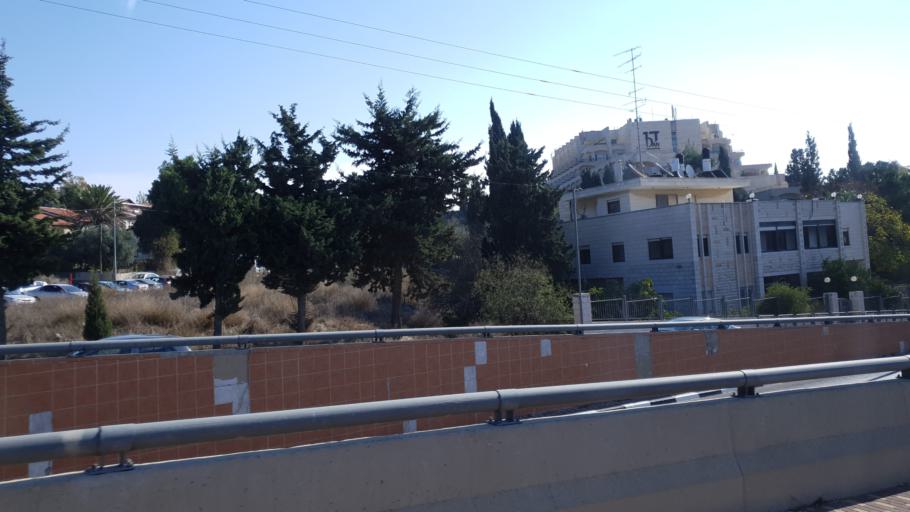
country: PS
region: West Bank
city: East Jerusalem
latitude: 31.7986
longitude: 35.2341
